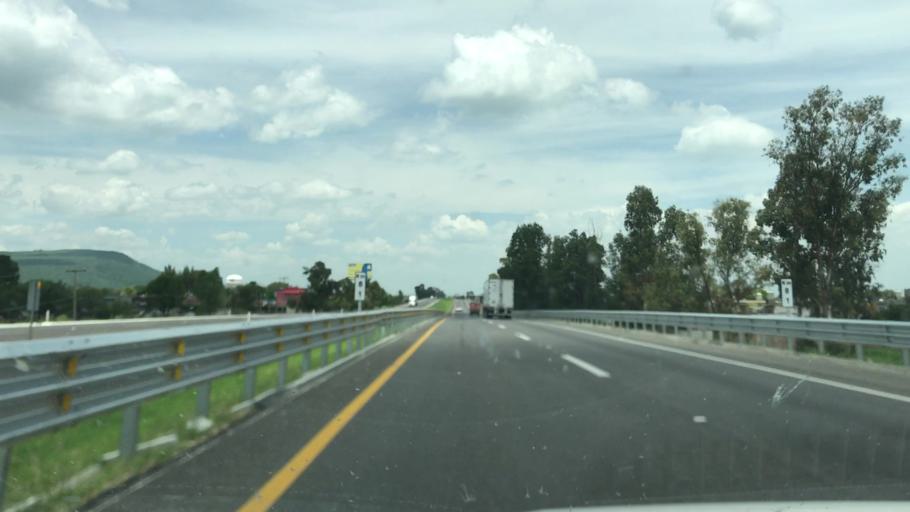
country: MX
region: Guanajuato
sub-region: Salamanca
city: El Divisador
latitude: 20.5949
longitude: -101.1634
